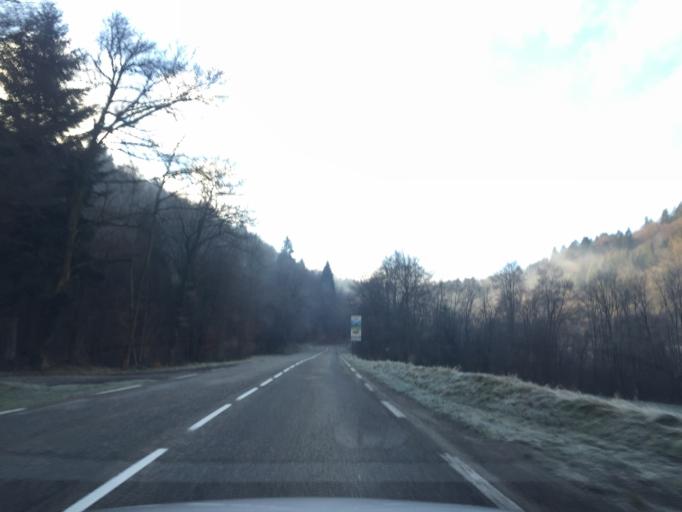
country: FR
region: Rhone-Alpes
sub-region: Departement de la Haute-Savoie
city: Gruffy
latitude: 45.7281
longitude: 6.0957
